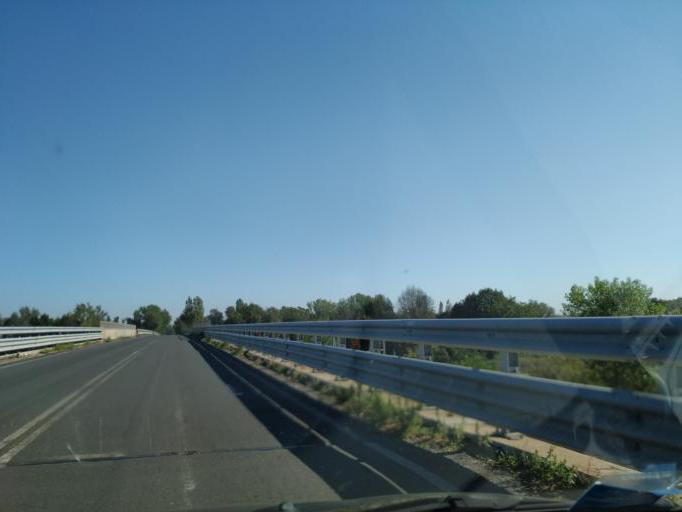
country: IT
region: Emilia-Romagna
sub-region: Provincia di Bologna
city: San Giovanni in Persiceto
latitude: 44.6557
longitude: 11.1803
